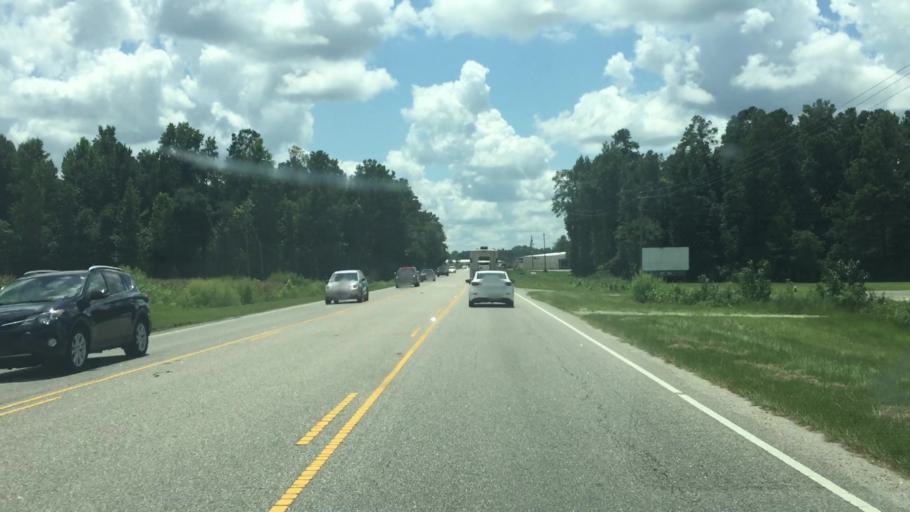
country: US
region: North Carolina
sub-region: Columbus County
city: Tabor City
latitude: 34.1503
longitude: -78.8614
